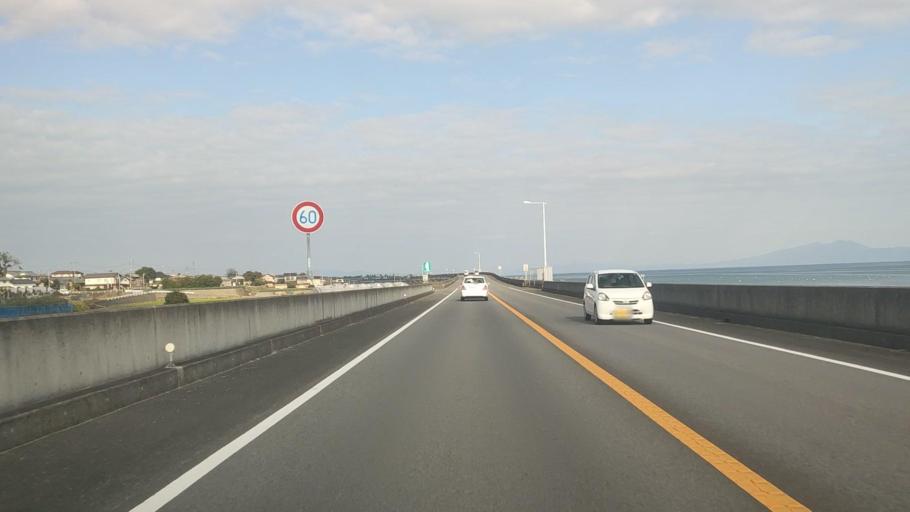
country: JP
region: Nagasaki
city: Shimabara
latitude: 32.7251
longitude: 130.3622
